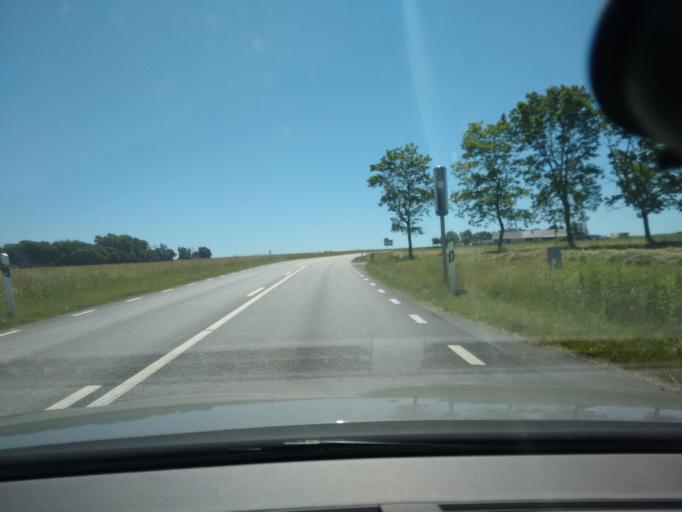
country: SE
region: Skane
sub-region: Horby Kommun
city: Hoerby
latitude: 55.8233
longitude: 13.6631
